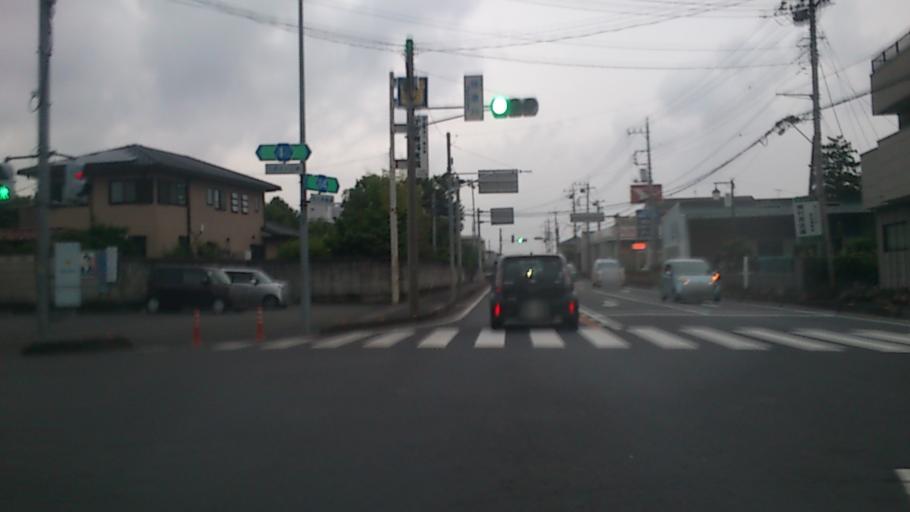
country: JP
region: Saitama
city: Kazo
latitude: 36.1550
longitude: 139.6209
